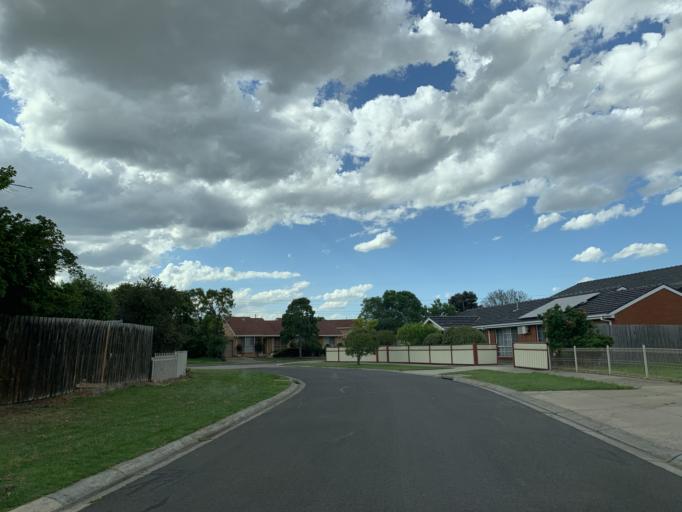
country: AU
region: Victoria
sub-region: Moonee Valley
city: Keilor East
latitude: -37.7426
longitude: 144.8558
